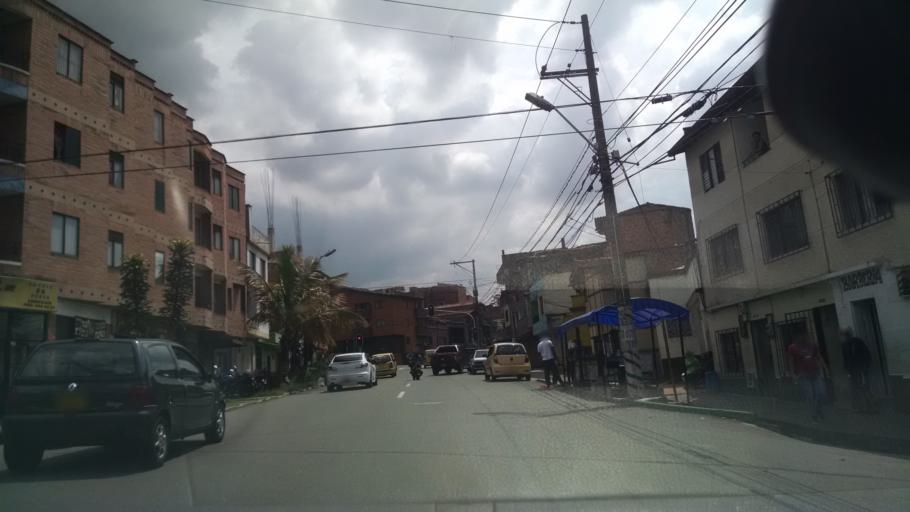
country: CO
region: Antioquia
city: Medellin
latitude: 6.2654
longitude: -75.5564
